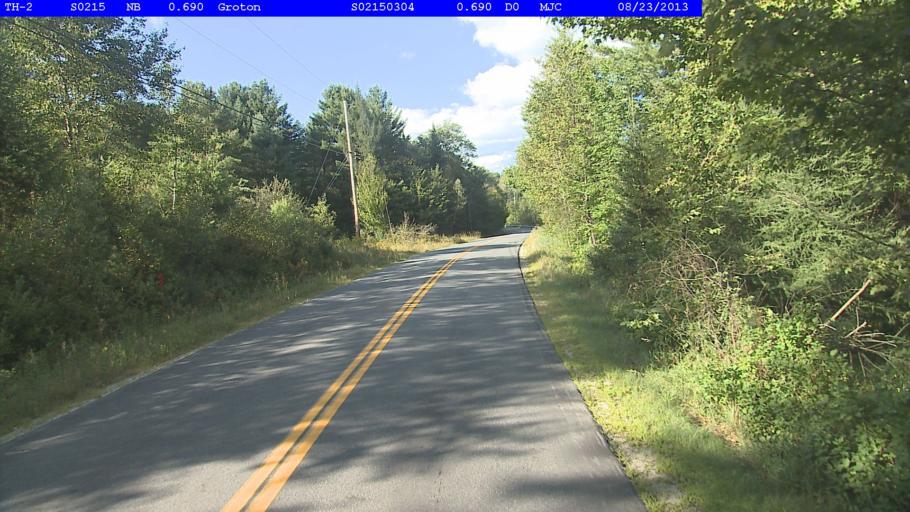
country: US
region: New Hampshire
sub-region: Grafton County
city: Woodsville
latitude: 44.2189
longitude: -72.1917
